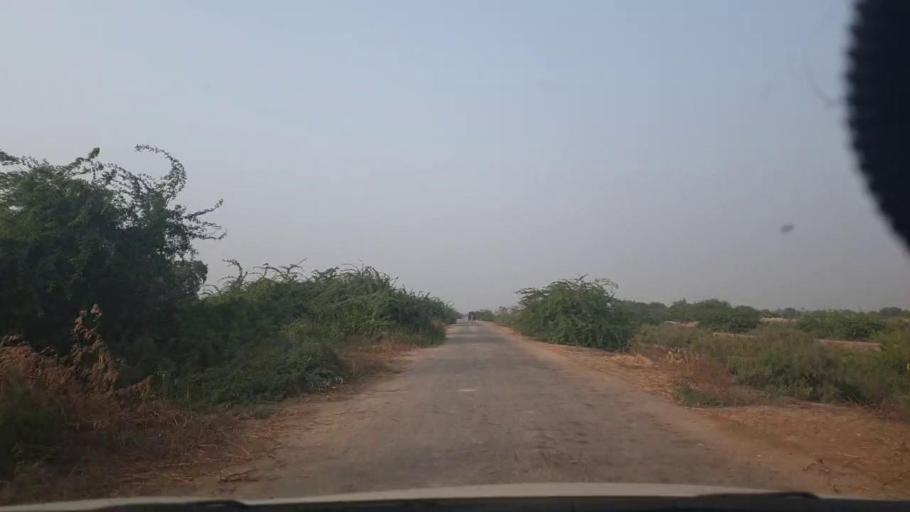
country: PK
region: Sindh
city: Bulri
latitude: 24.8238
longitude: 68.4032
